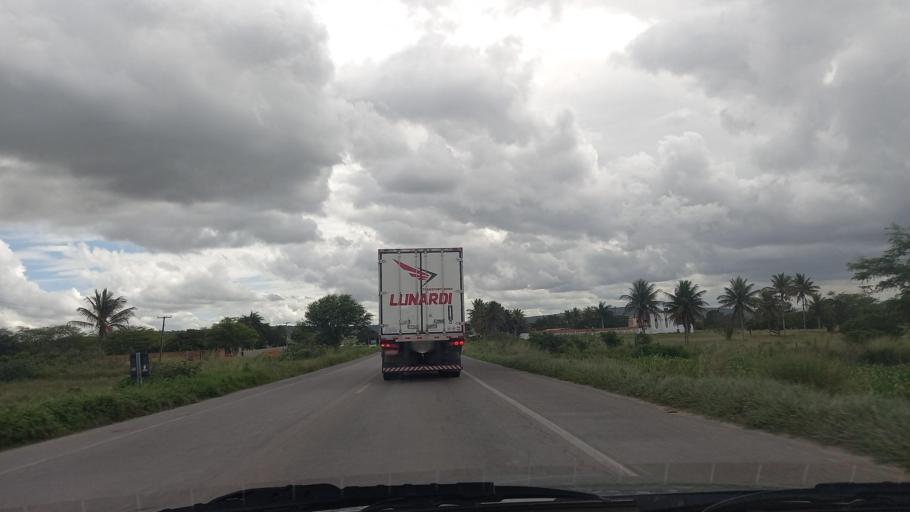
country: BR
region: Pernambuco
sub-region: Lajedo
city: Lajedo
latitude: -8.6618
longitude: -36.3452
